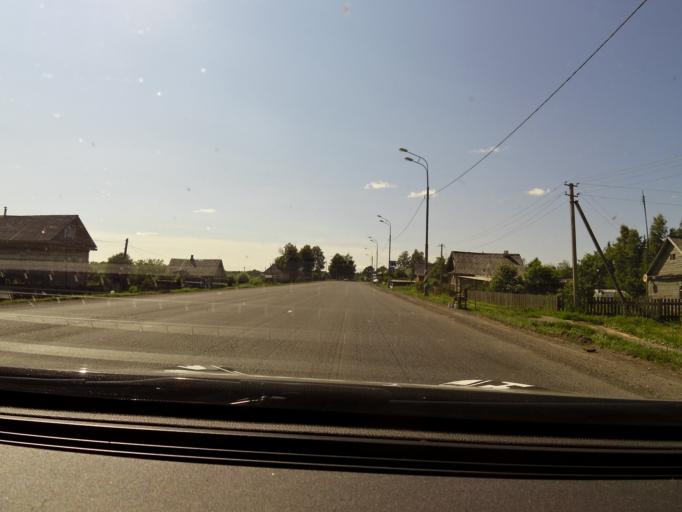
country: RU
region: Novgorod
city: Proletariy
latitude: 58.3671
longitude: 32.0725
